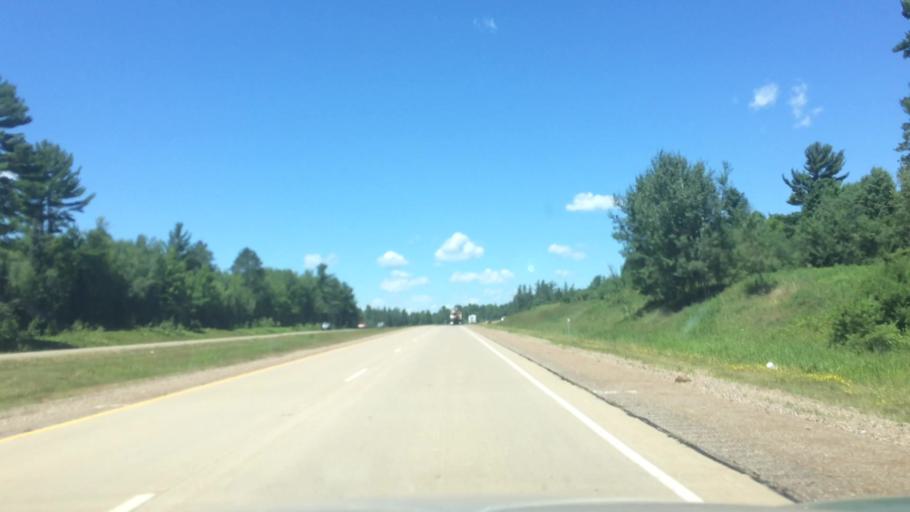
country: US
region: Wisconsin
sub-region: Lincoln County
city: Tomahawk
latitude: 45.4403
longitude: -89.6831
